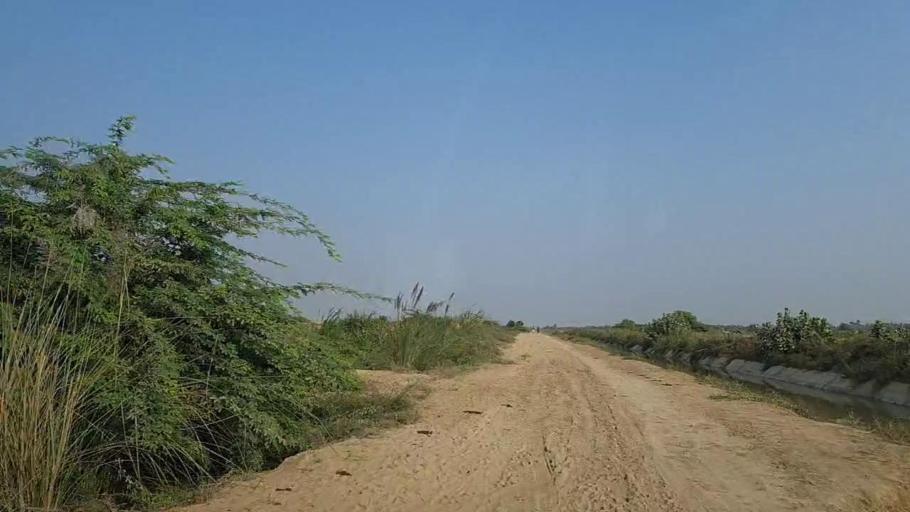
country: PK
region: Sindh
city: Mirpur Sakro
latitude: 24.6154
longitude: 67.7090
